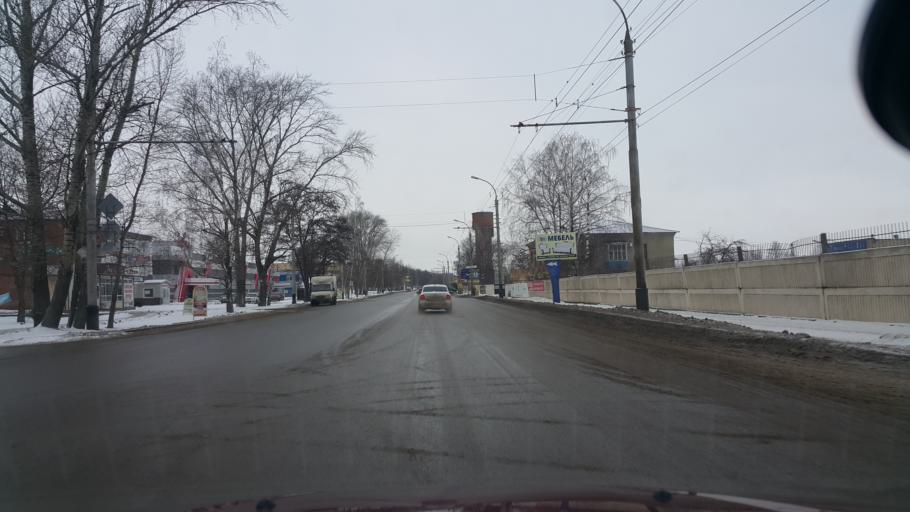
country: RU
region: Tambov
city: Tambov
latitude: 52.7337
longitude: 41.3989
